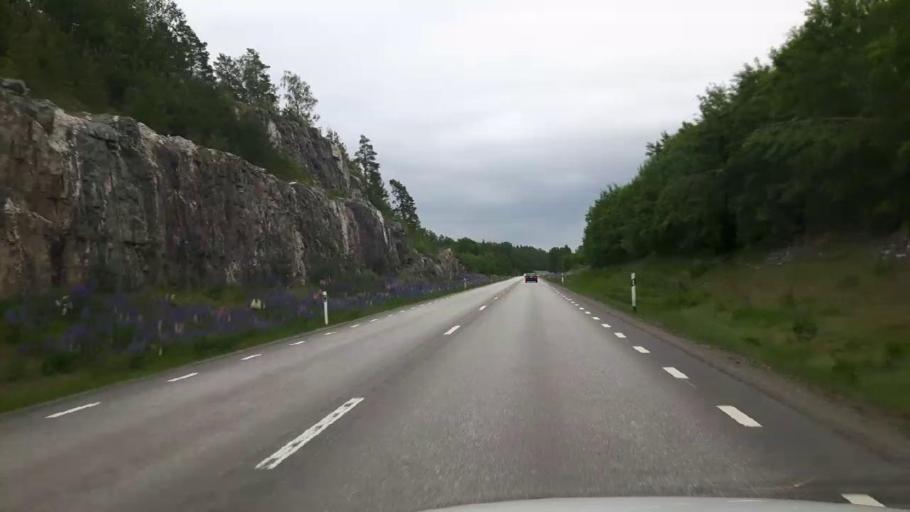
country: SE
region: Vaestmanland
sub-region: Kopings Kommun
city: Kolsva
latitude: 59.5649
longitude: 15.8855
